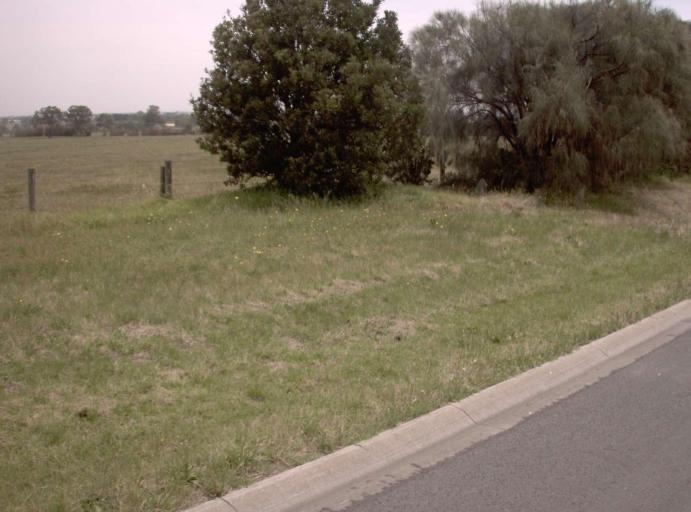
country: AU
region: Victoria
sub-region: Casey
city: Lynbrook
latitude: -38.0582
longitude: 145.2430
